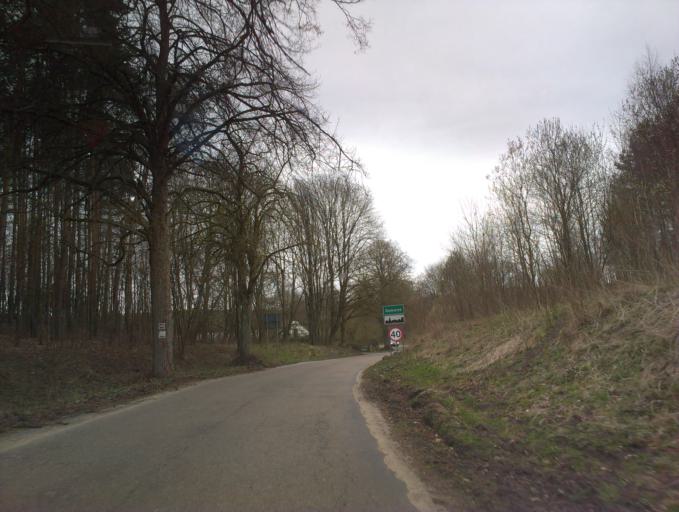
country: PL
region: West Pomeranian Voivodeship
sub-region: Powiat szczecinecki
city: Lubowo
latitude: 53.6277
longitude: 16.3451
